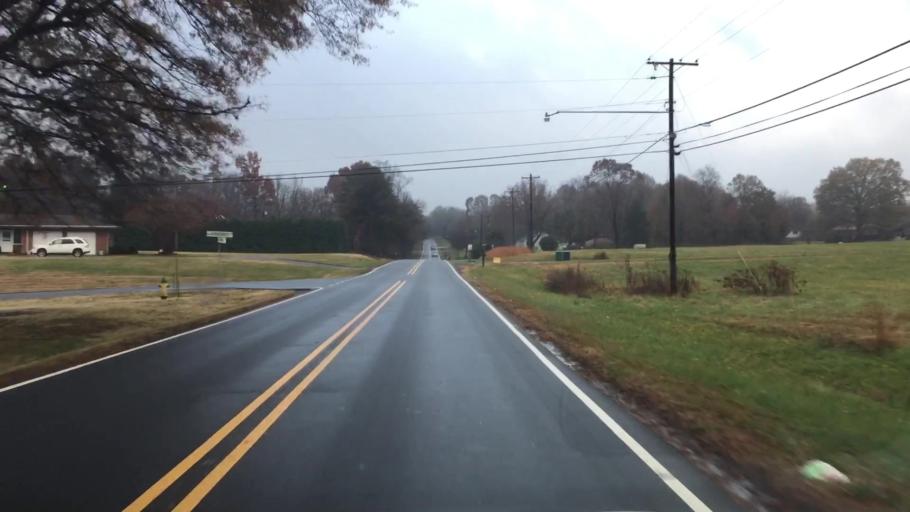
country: US
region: North Carolina
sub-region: Rockingham County
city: Reidsville
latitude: 36.3447
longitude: -79.6995
